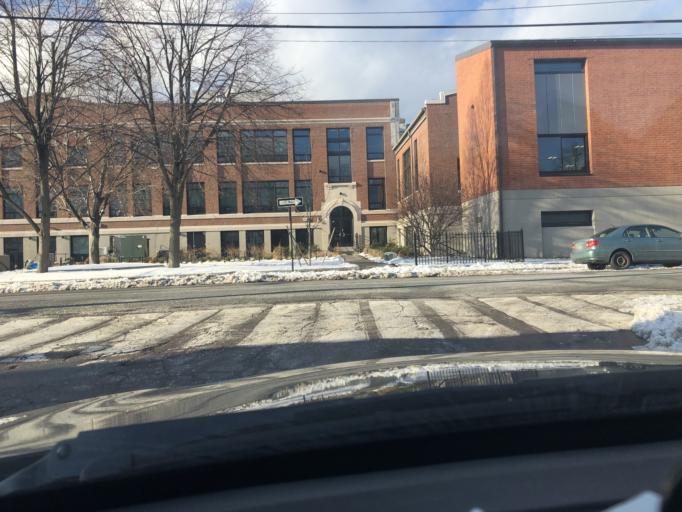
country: US
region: Massachusetts
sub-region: Middlesex County
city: Arlington
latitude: 42.4103
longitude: -71.1446
